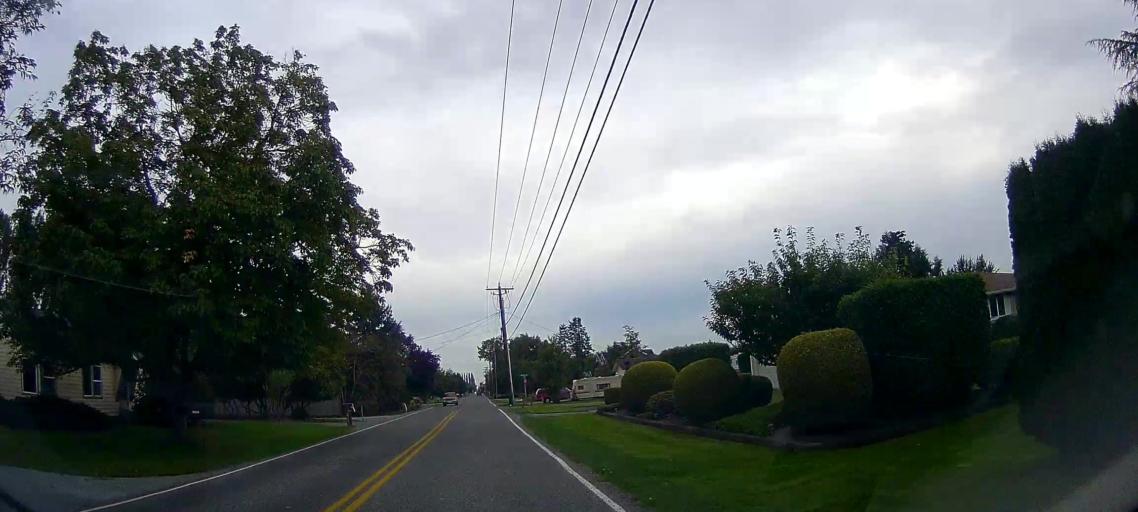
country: US
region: Washington
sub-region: Skagit County
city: Mount Vernon
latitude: 48.4407
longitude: -122.3787
